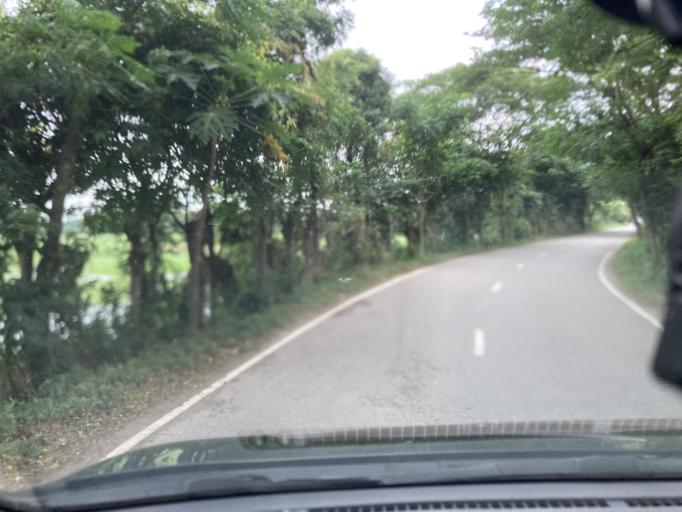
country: BD
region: Dhaka
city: Azimpur
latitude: 23.7787
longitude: 90.2075
